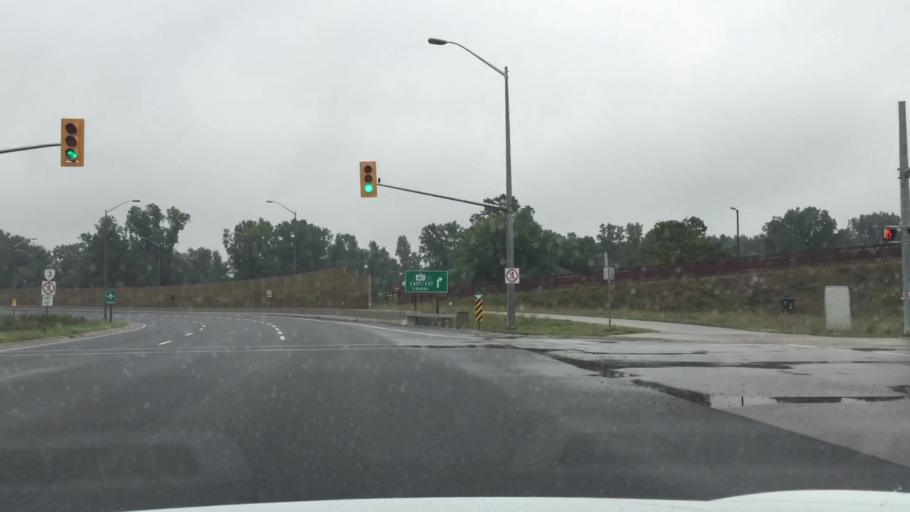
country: CA
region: Ontario
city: Windsor
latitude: 42.2661
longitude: -83.0459
